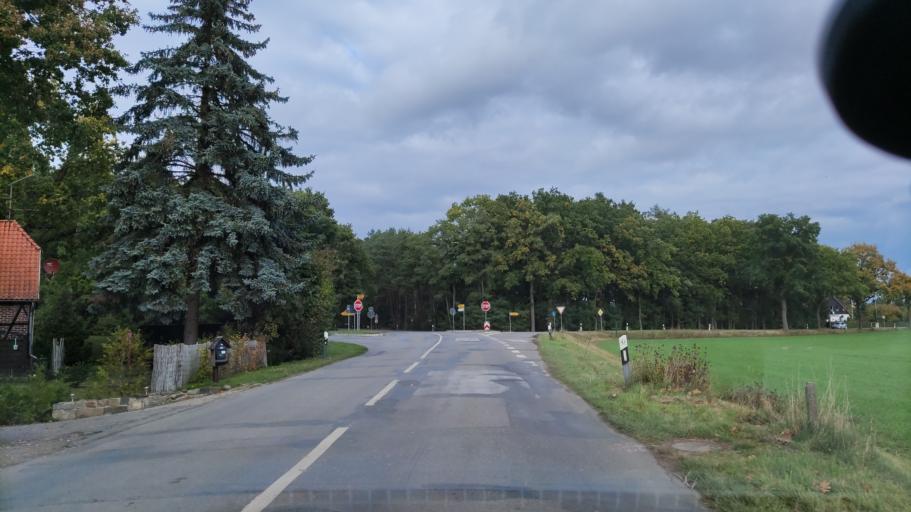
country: DE
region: Lower Saxony
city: Romstedt
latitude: 53.0712
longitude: 10.6266
